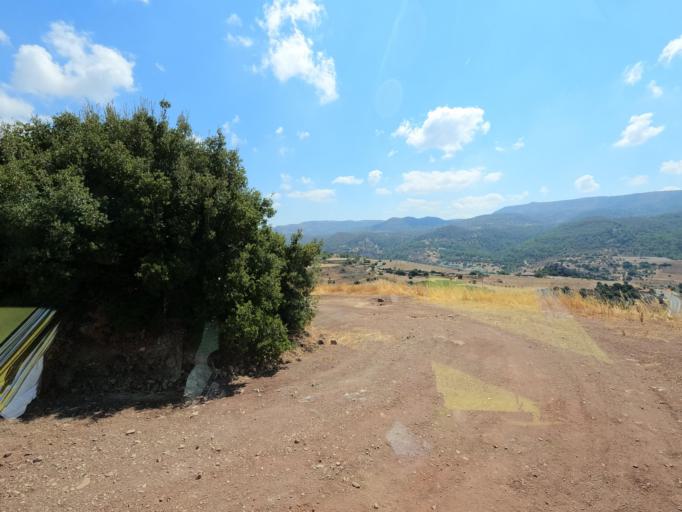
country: CY
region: Limassol
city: Pachna
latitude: 34.7934
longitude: 32.6860
